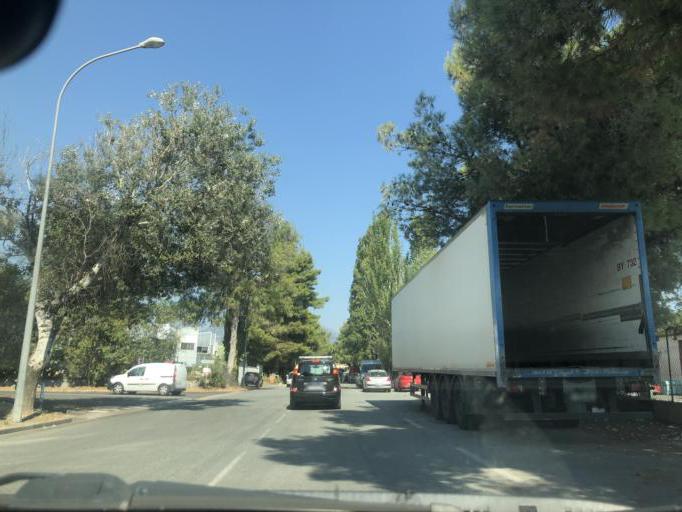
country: FR
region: Provence-Alpes-Cote d'Azur
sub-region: Departement des Alpes-Maritimes
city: Castagniers
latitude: 43.7837
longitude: 7.2112
